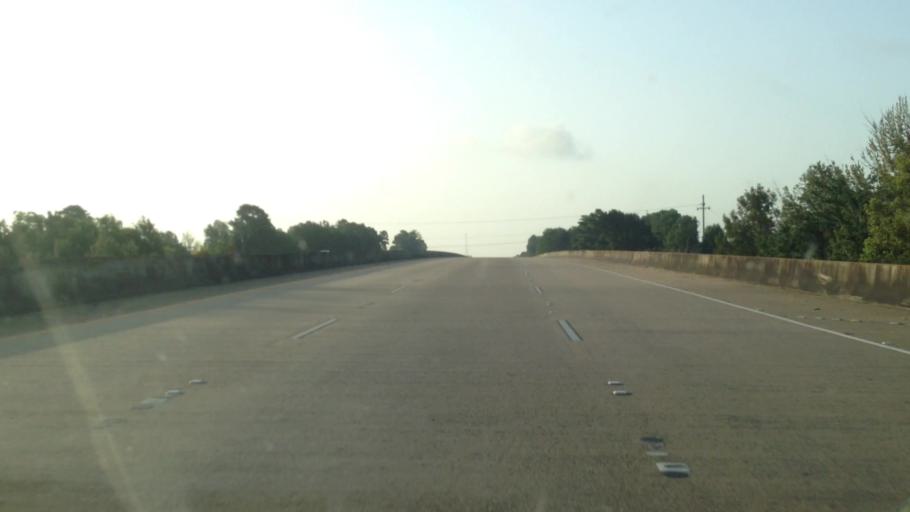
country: US
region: Louisiana
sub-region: Rapides Parish
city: Boyce
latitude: 31.4064
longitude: -92.7128
